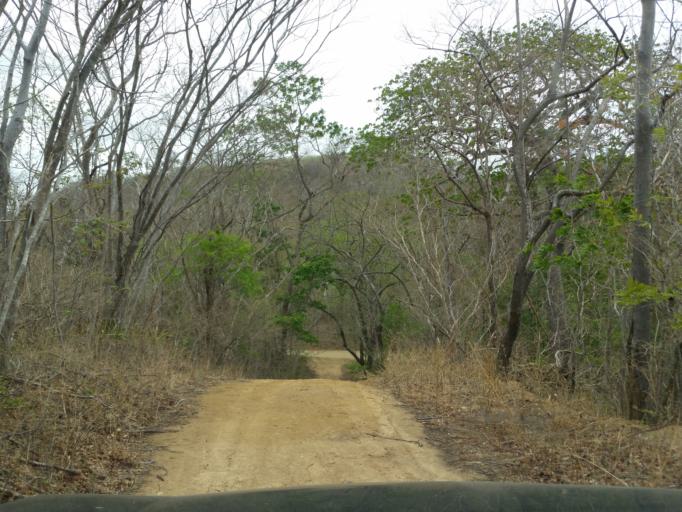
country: NI
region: Rivas
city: Tola
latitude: 11.4300
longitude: -86.0714
